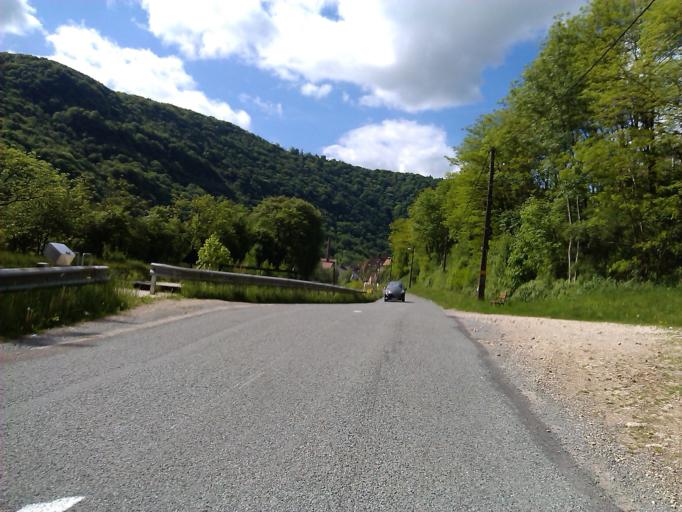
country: FR
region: Franche-Comte
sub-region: Departement du Doubs
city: Roulans
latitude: 47.2988
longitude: 6.2052
